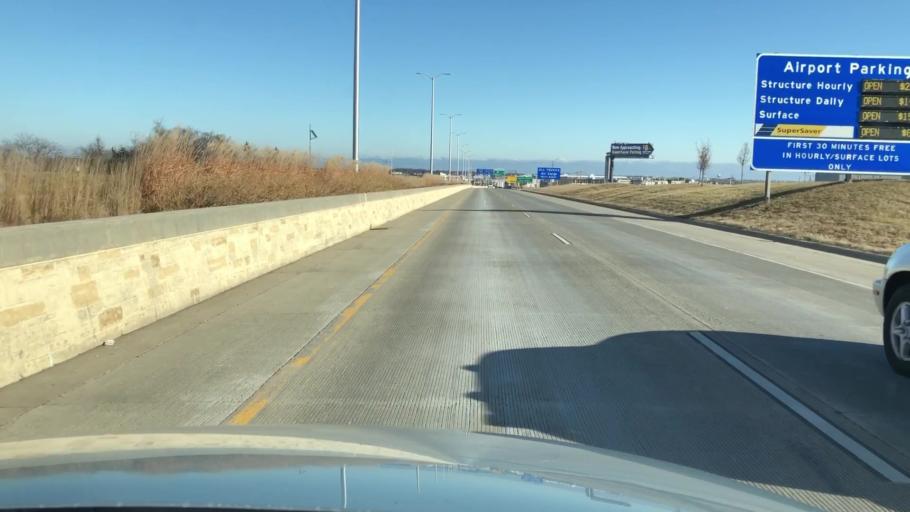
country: US
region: Wisconsin
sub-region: Milwaukee County
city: Saint Francis
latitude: 42.9428
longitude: -87.9228
